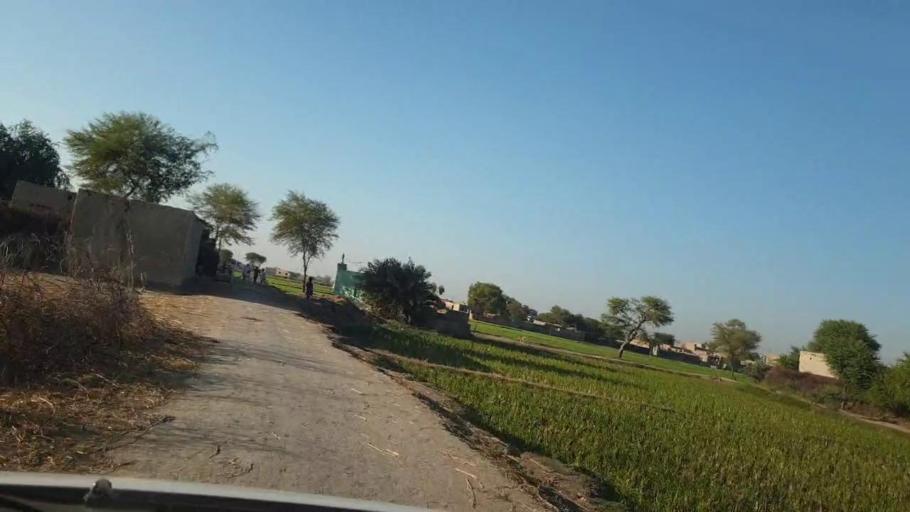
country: PK
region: Sindh
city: Khairpur Nathan Shah
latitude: 27.0423
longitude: 67.7285
